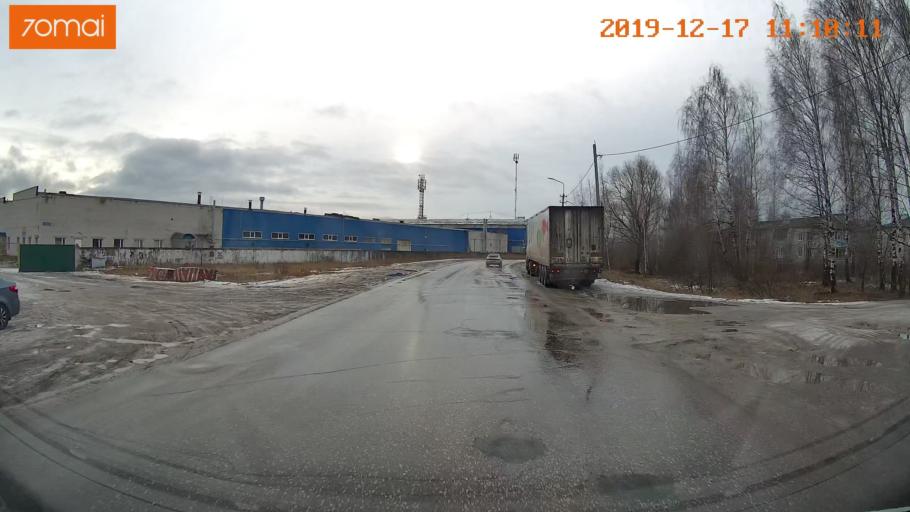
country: RU
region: Vladimir
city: Gus'-Khrustal'nyy
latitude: 55.5946
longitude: 40.6422
